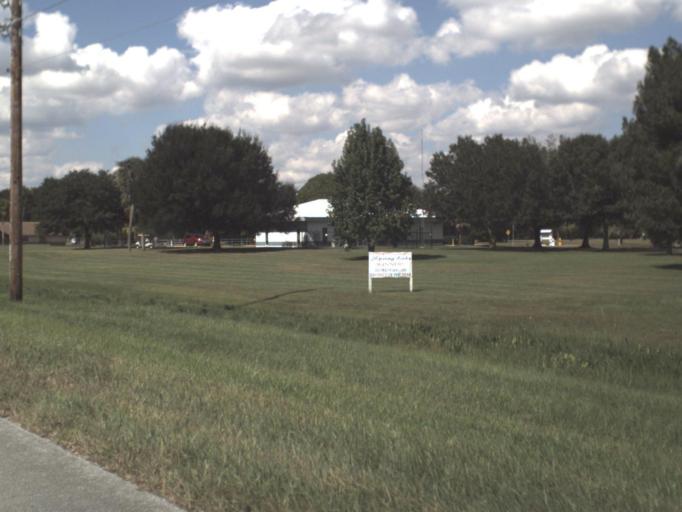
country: US
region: Florida
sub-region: Highlands County
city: Sebring
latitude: 27.4339
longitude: -81.3335
